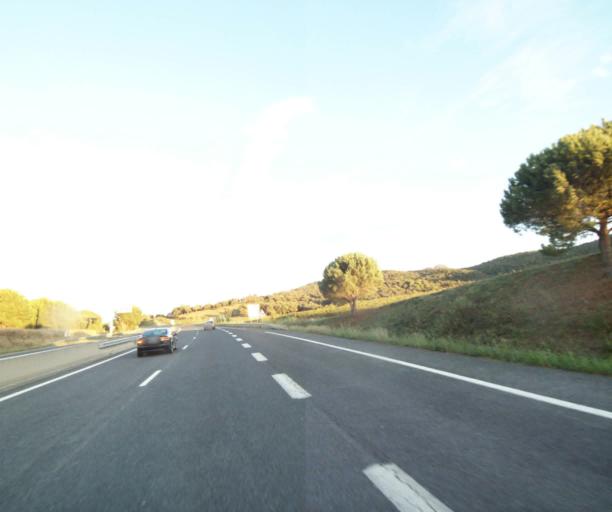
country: FR
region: Languedoc-Roussillon
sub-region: Departement des Pyrenees-Orientales
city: Argelers
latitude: 42.5358
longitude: 3.0337
